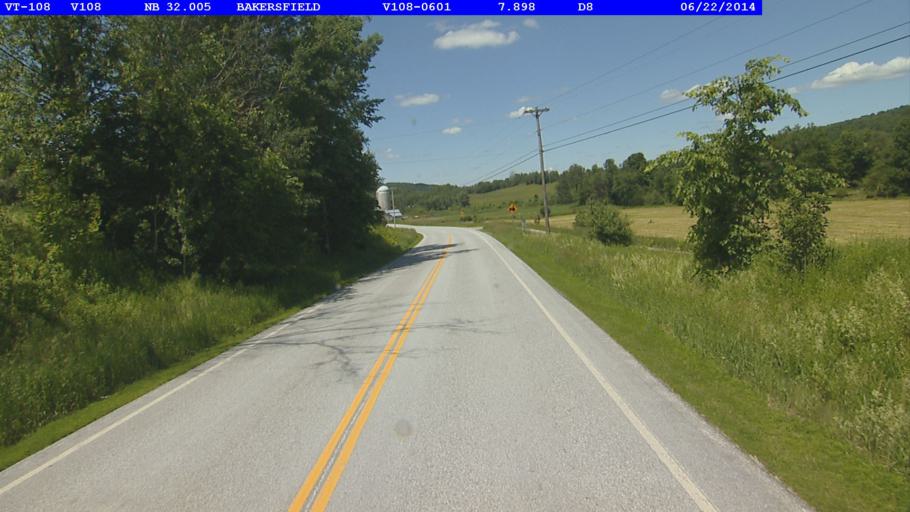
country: US
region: Vermont
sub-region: Franklin County
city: Enosburg Falls
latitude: 44.8366
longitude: -72.8046
